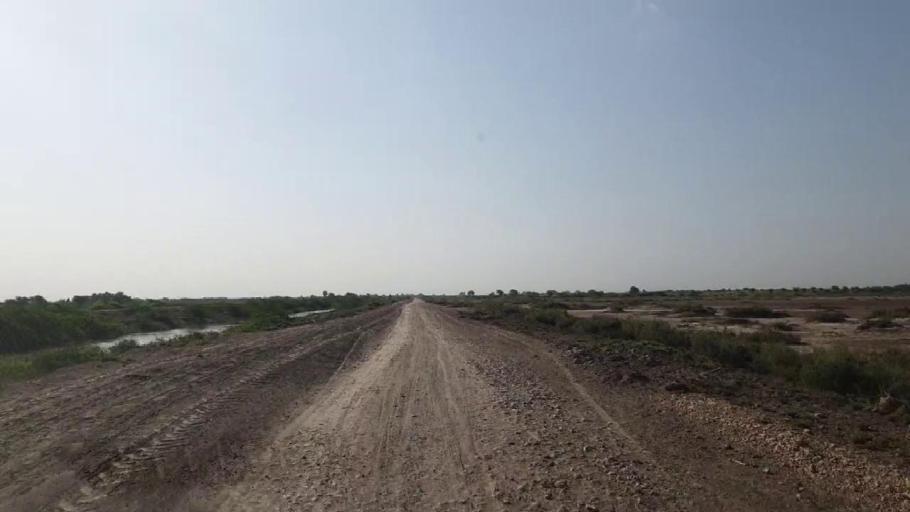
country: PK
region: Sindh
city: Kadhan
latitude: 24.6321
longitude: 69.0728
